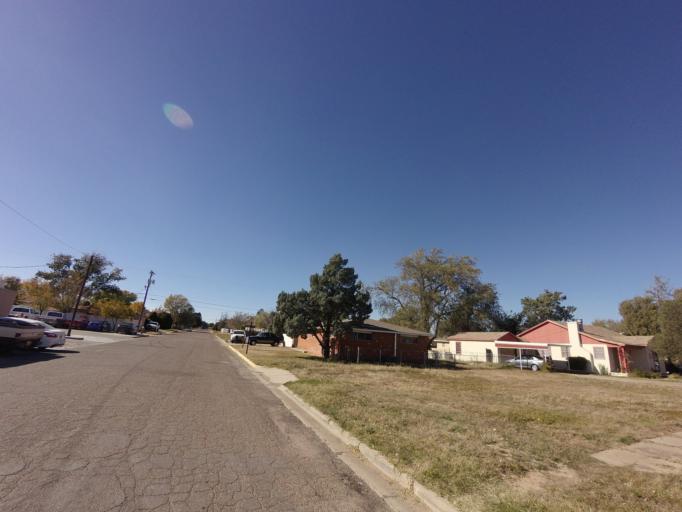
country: US
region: New Mexico
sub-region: Curry County
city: Clovis
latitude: 34.4285
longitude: -103.1967
